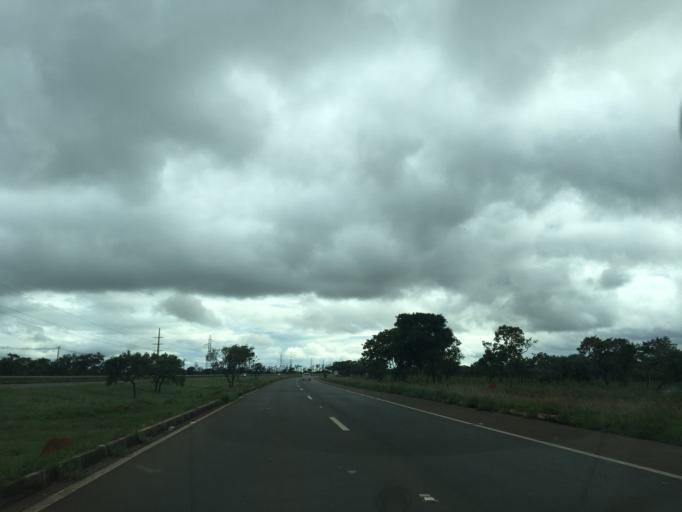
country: BR
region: Federal District
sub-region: Brasilia
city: Brasilia
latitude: -15.9046
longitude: -47.8203
